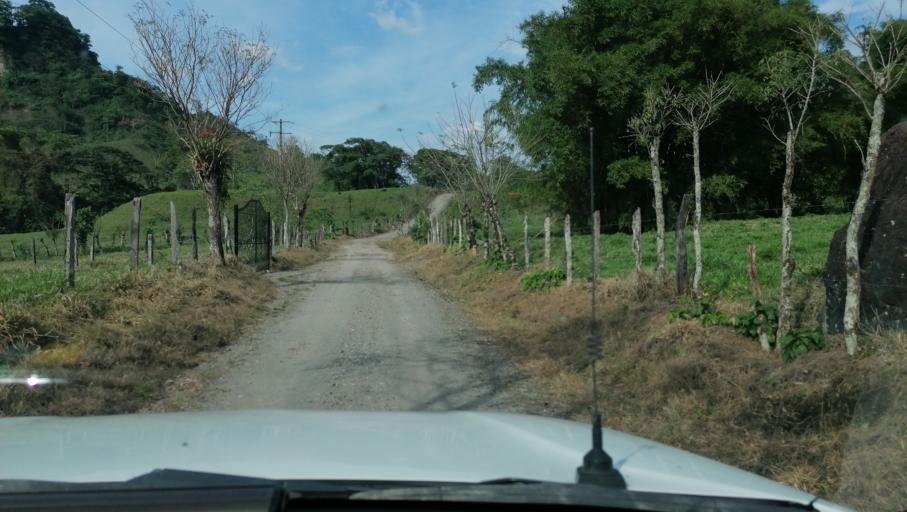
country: MX
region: Chiapas
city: Ostuacan
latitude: 17.4612
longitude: -93.2405
